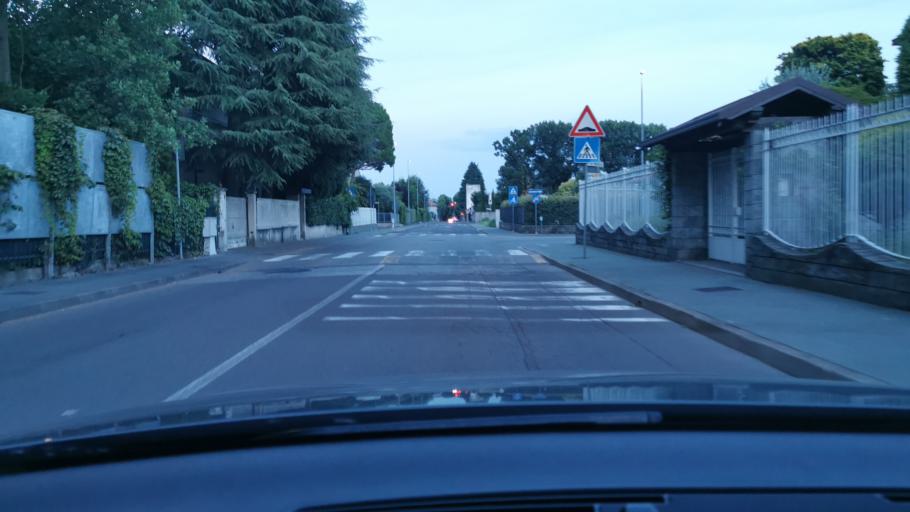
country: IT
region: Lombardy
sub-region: Citta metropolitana di Milano
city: Rescaldina
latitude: 45.6209
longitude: 8.9527
